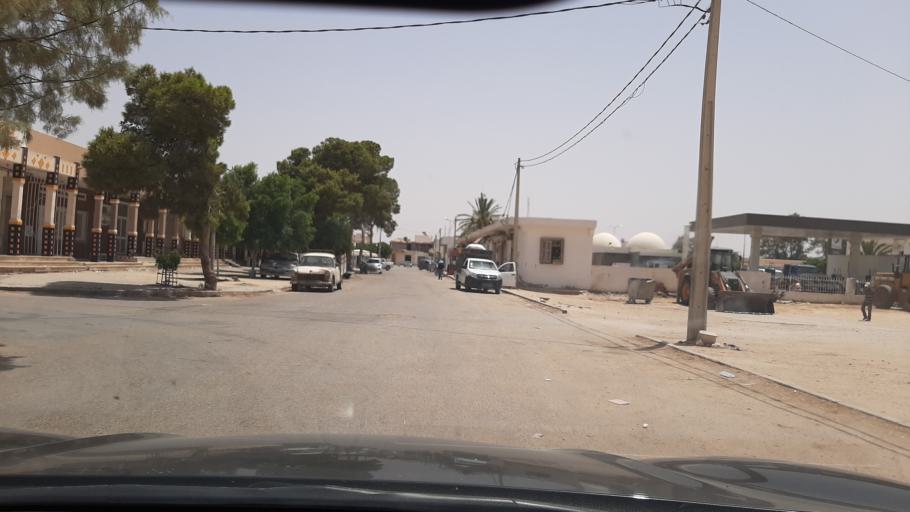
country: TN
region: Qabis
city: Gabes
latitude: 33.6182
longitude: 10.2878
